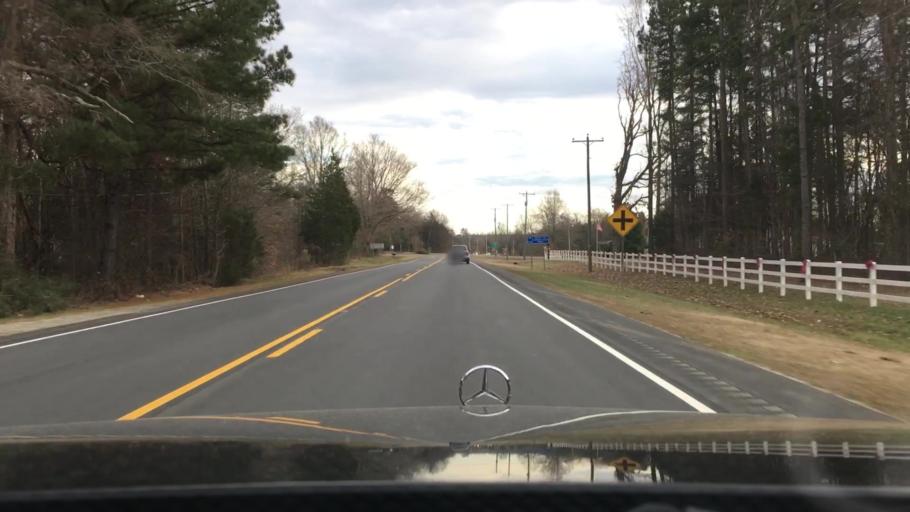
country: US
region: North Carolina
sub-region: Alamance County
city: Mebane
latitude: 36.2514
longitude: -79.1913
